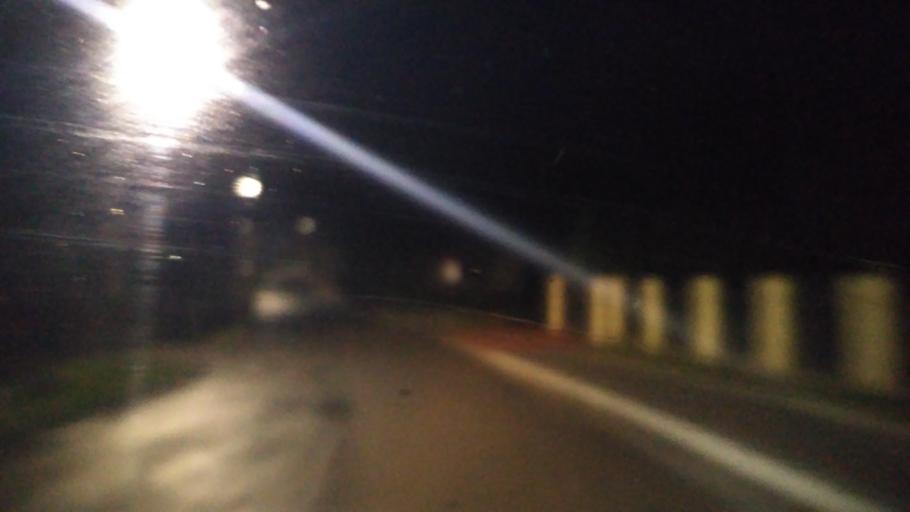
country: PL
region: Subcarpathian Voivodeship
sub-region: Powiat jaroslawski
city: Pruchnik
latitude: 49.9401
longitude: 22.5255
